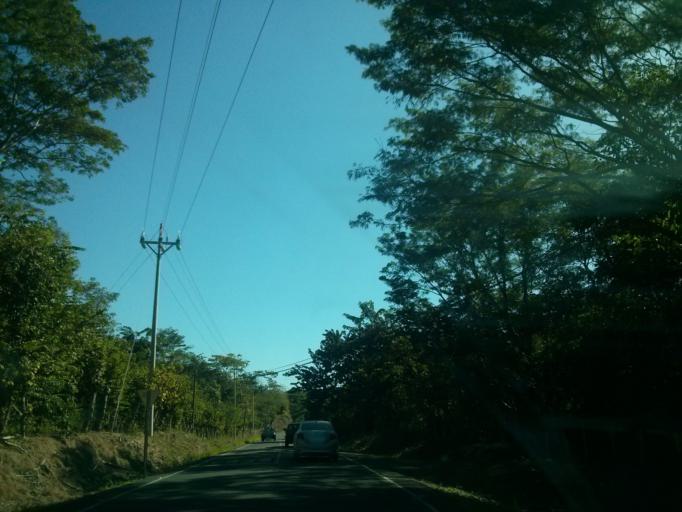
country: CR
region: Puntarenas
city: Paquera
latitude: 9.7342
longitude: -85.0230
